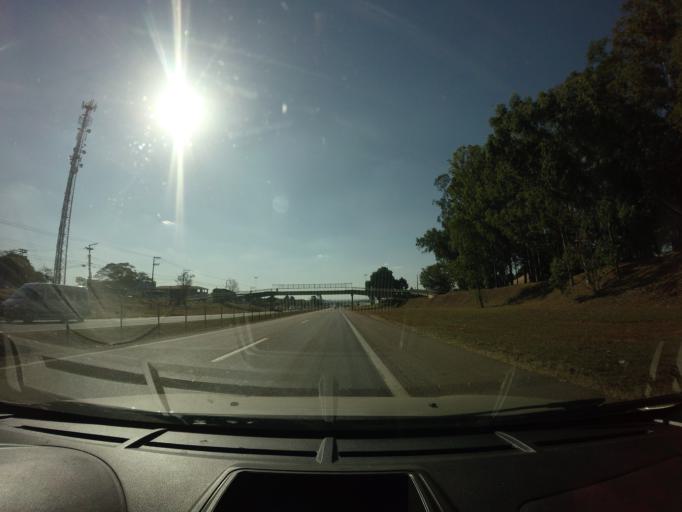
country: BR
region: Sao Paulo
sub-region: Piracicaba
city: Piracicaba
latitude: -22.7574
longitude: -47.5970
